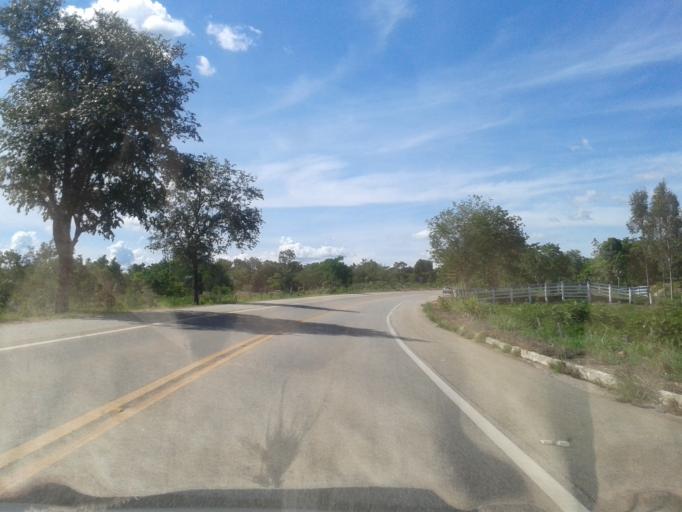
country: BR
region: Goias
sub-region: Itapuranga
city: Itapuranga
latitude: -15.3889
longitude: -50.3897
